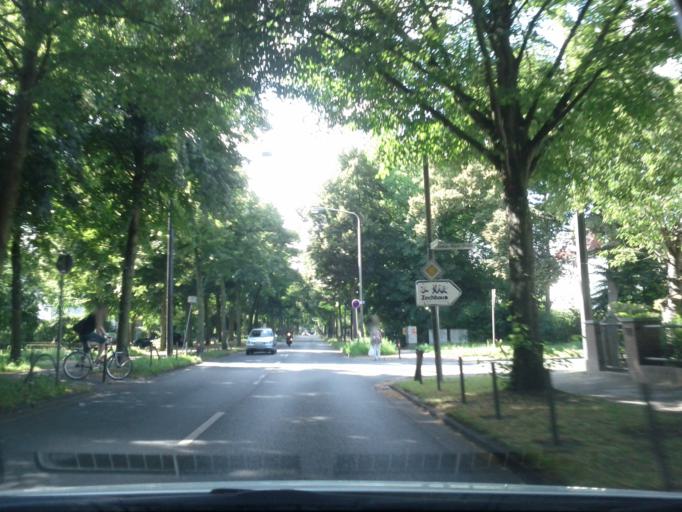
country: DE
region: Bremen
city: Bremen
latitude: 53.0901
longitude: 8.8393
